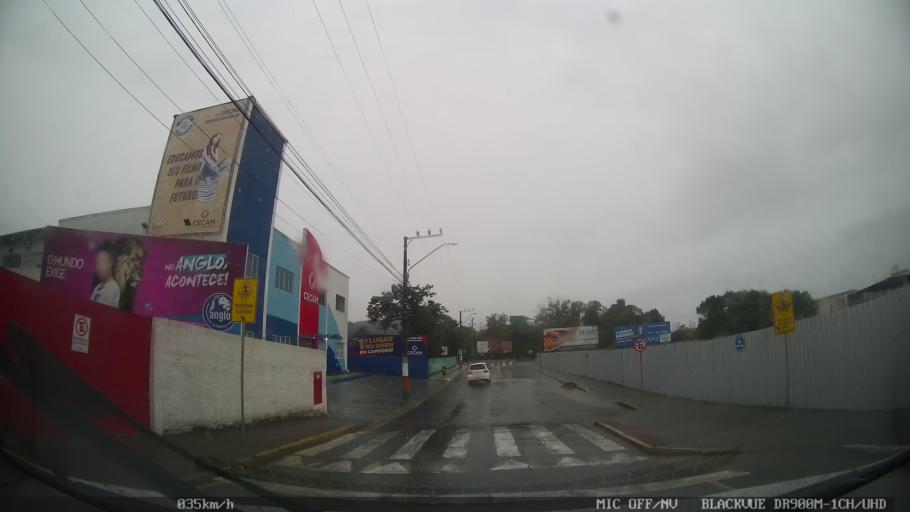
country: BR
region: Santa Catarina
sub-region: Balneario Camboriu
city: Balneario Camboriu
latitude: -27.0199
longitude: -48.6505
